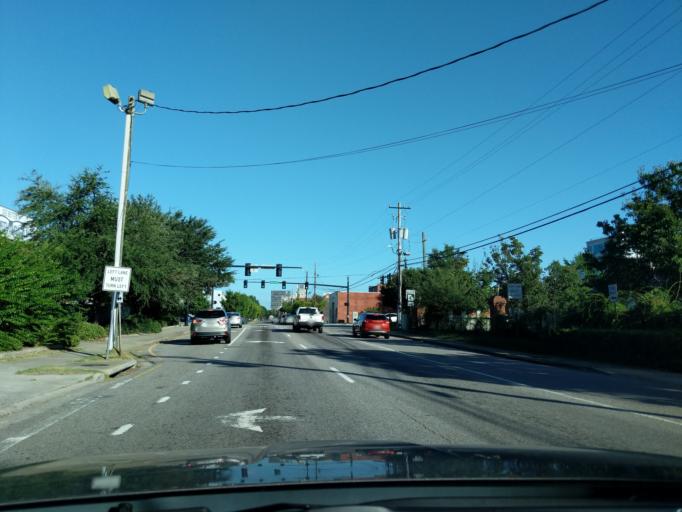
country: US
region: Georgia
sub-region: Richmond County
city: Augusta
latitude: 33.4797
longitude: -81.9759
